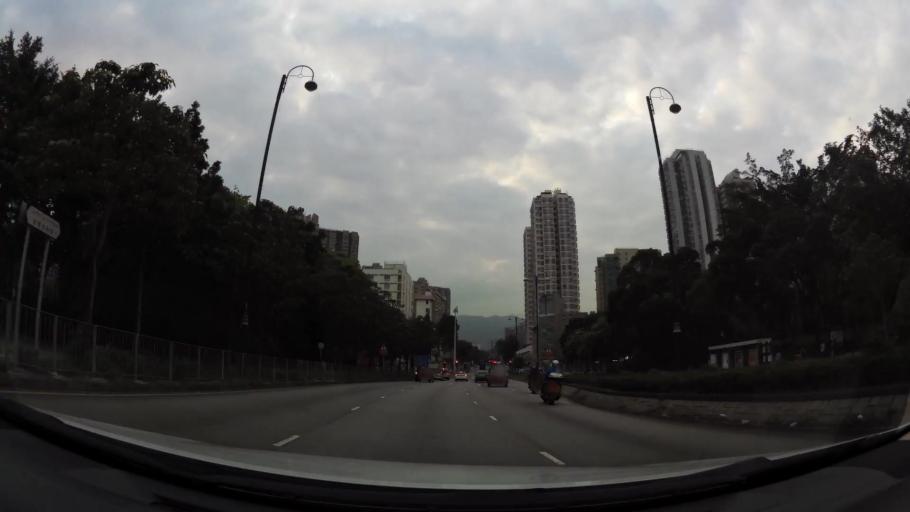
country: HK
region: Tai Po
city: Tai Po
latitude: 22.4510
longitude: 114.1661
